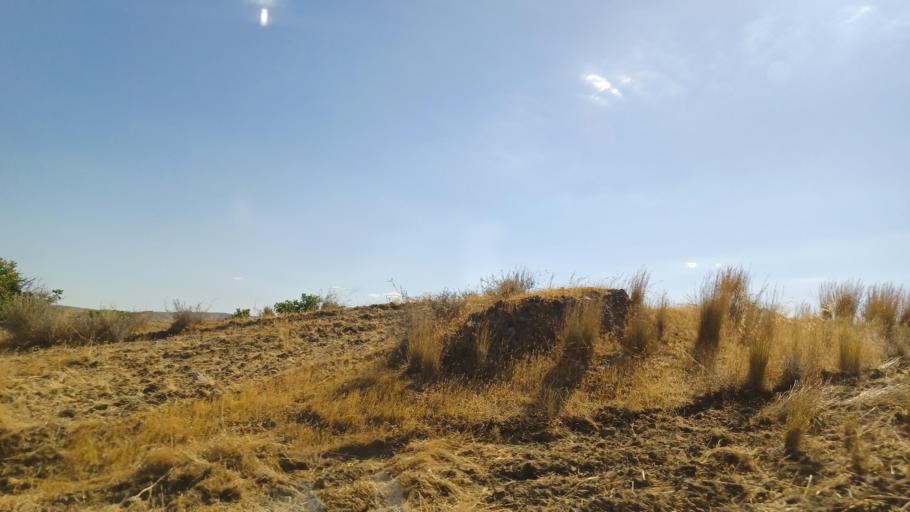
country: CY
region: Larnaka
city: Troulloi
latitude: 35.0061
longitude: 33.5885
